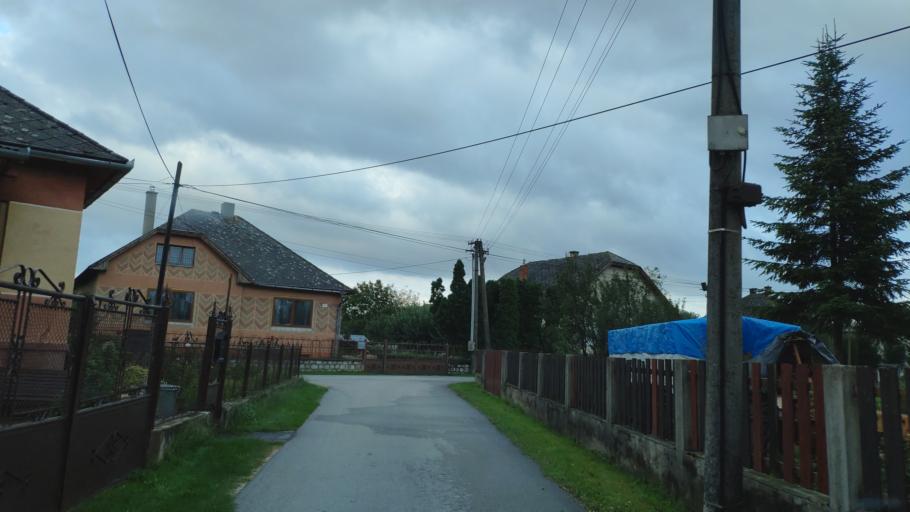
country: SK
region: Kosicky
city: Moldava nad Bodvou
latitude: 48.5775
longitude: 20.9545
